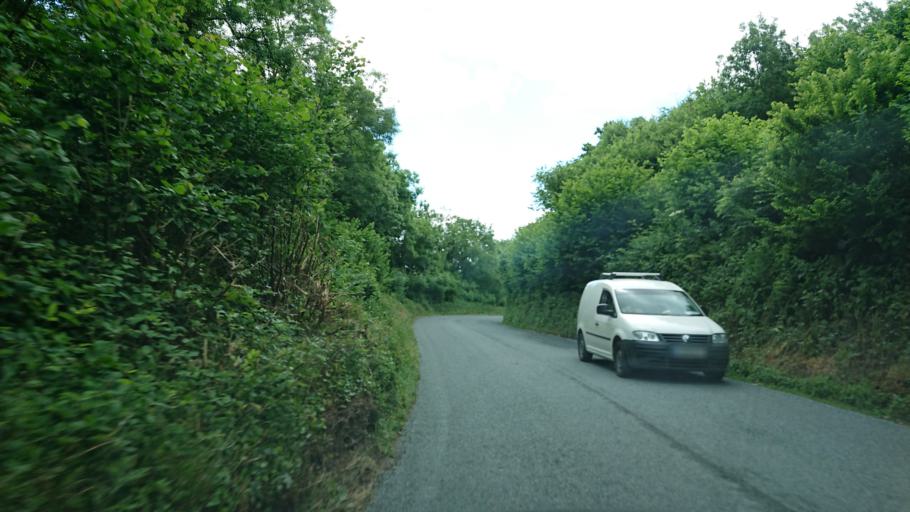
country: IE
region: Munster
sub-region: Waterford
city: Tra Mhor
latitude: 52.1773
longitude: -7.1485
